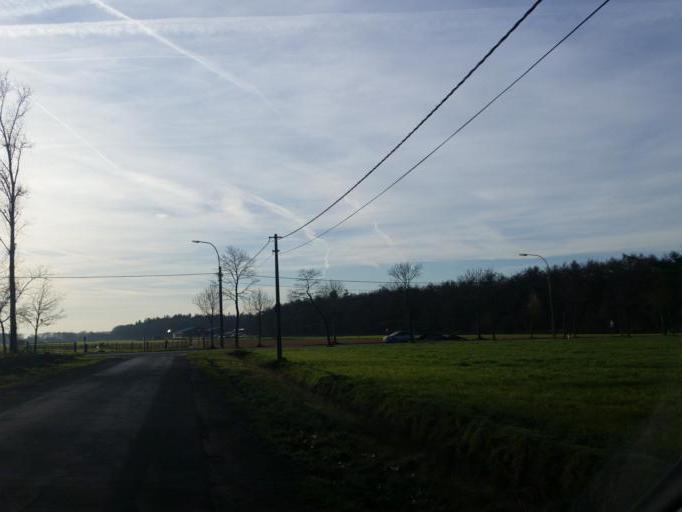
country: BE
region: Flanders
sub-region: Provincie Oost-Vlaanderen
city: Kaprijke
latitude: 51.1879
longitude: 3.6599
